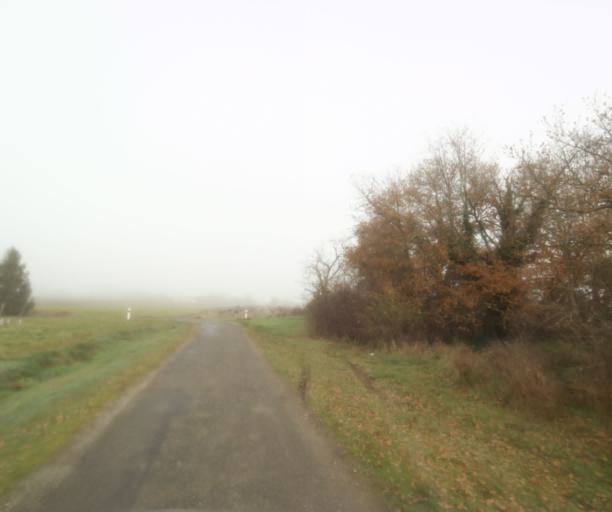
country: FR
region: Midi-Pyrenees
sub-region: Departement de la Haute-Garonne
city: Villaudric
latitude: 43.8335
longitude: 1.4606
